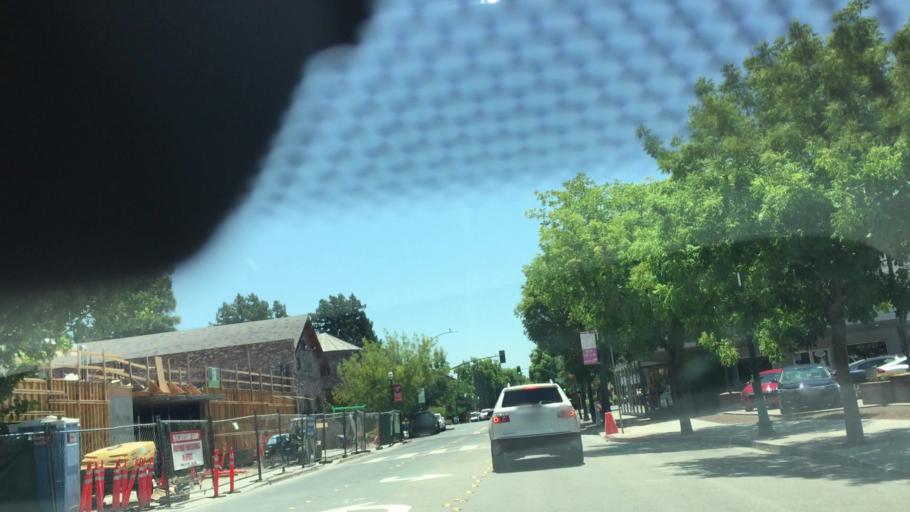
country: US
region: California
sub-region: Contra Costa County
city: Walnut Creek
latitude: 37.9027
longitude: -122.0625
